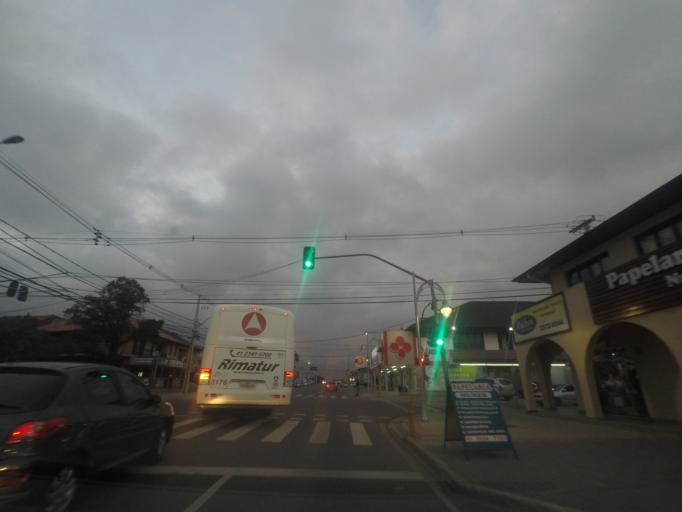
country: BR
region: Parana
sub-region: Almirante Tamandare
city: Almirante Tamandare
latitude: -25.3954
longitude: -49.3472
